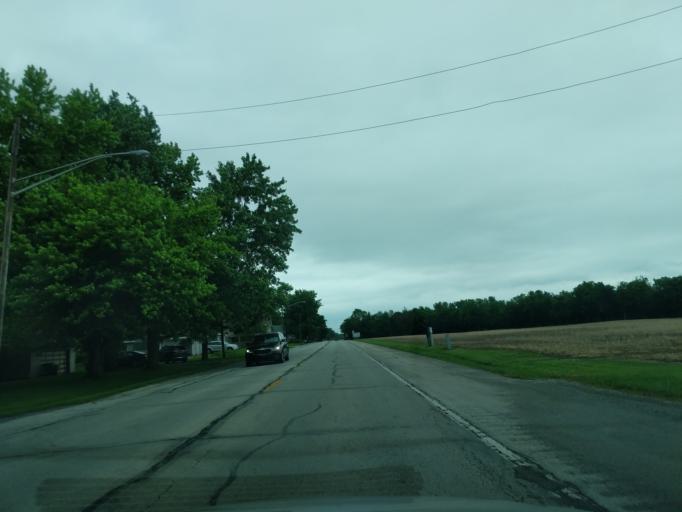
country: US
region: Indiana
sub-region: Hamilton County
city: Arcadia
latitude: 40.1712
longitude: -86.0130
